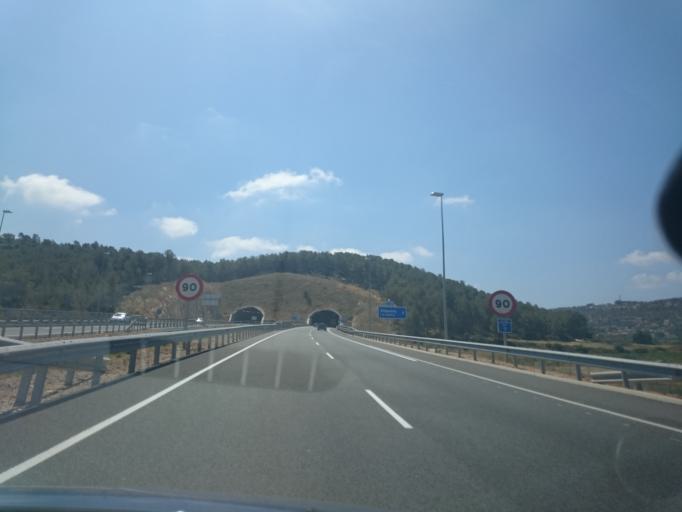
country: ES
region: Catalonia
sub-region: Provincia de Barcelona
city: Sant Pere de Ribes
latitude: 41.2867
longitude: 1.7270
